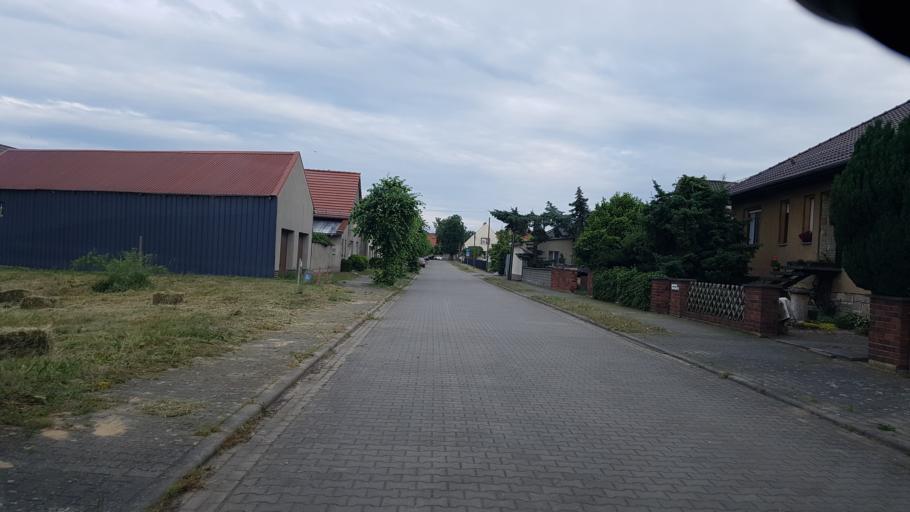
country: DE
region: Brandenburg
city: Schlieben
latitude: 51.7227
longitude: 13.4184
